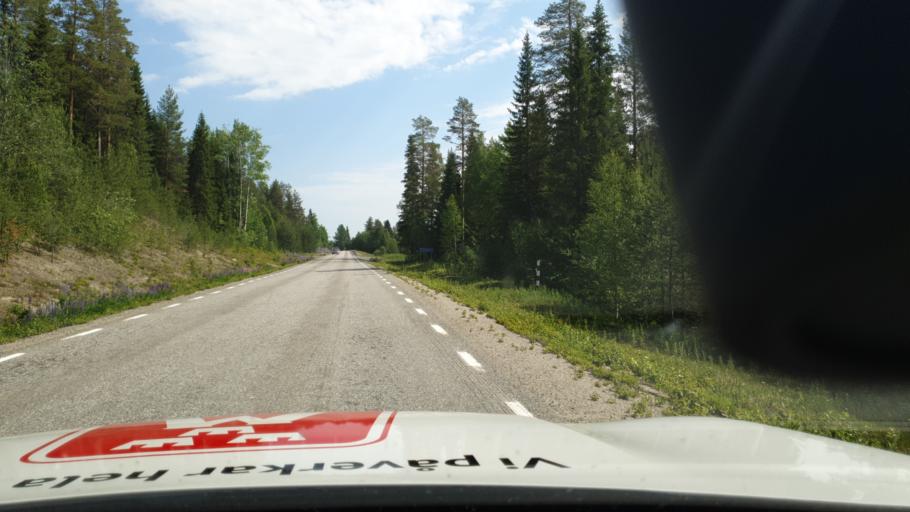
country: SE
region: Vaesterbotten
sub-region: Vindelns Kommun
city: Vindeln
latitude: 64.2535
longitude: 19.9106
